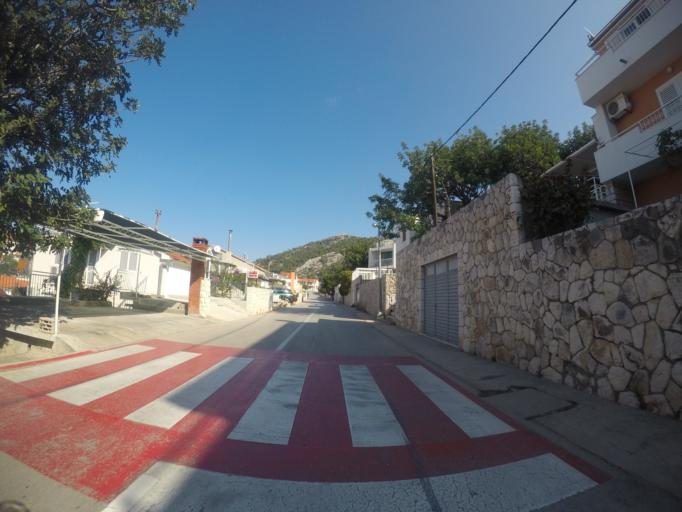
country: HR
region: Splitsko-Dalmatinska
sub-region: Grad Hvar
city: Hvar
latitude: 43.1689
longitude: 16.4461
